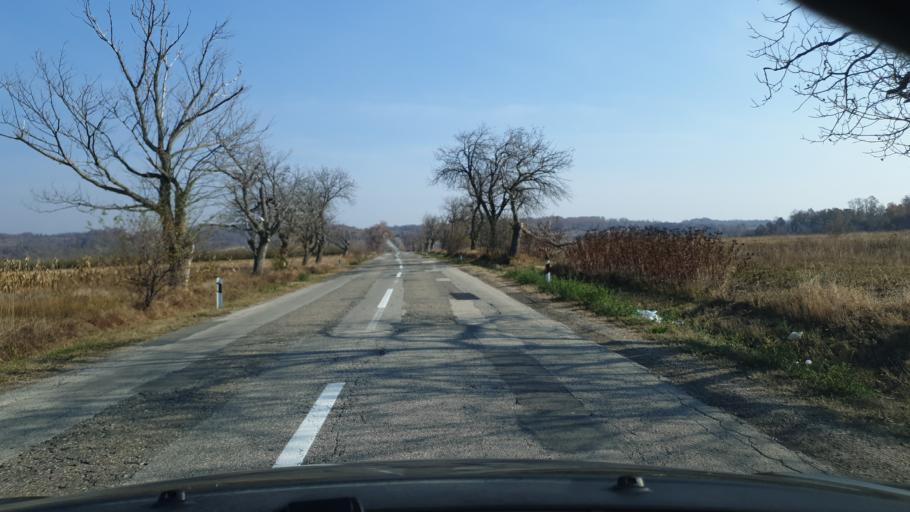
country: RS
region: Central Serbia
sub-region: Borski Okrug
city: Negotin
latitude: 44.2089
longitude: 22.4347
